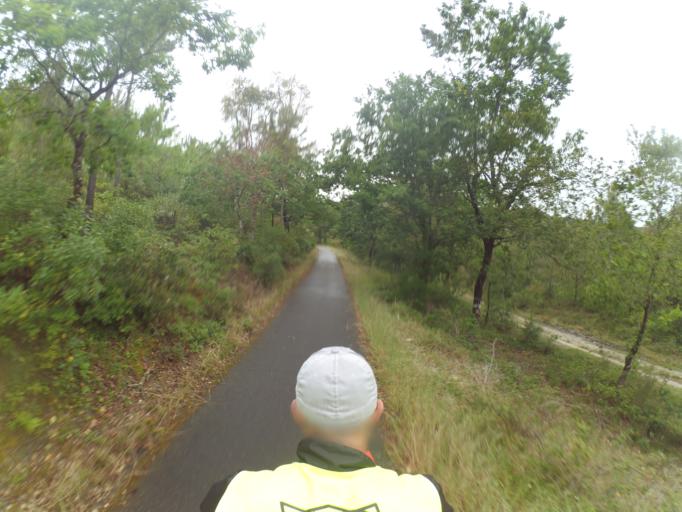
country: FR
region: Aquitaine
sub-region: Departement des Landes
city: Mimizan
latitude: 44.2192
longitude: -1.2394
